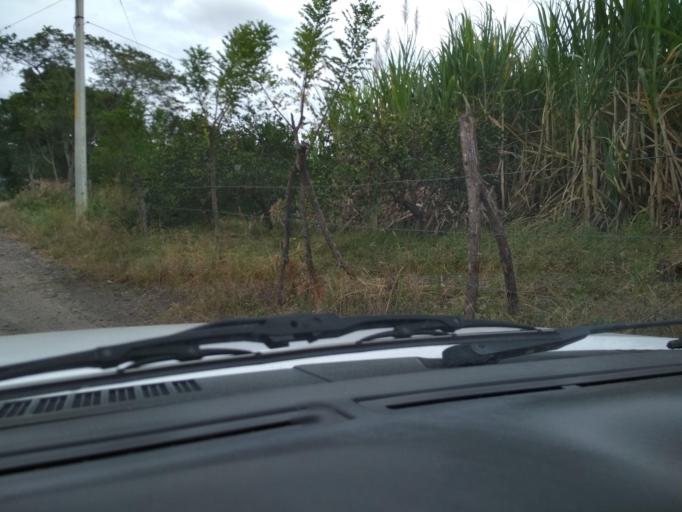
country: MX
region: Veracruz
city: Alto Lucero
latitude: 19.5946
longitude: -96.7825
